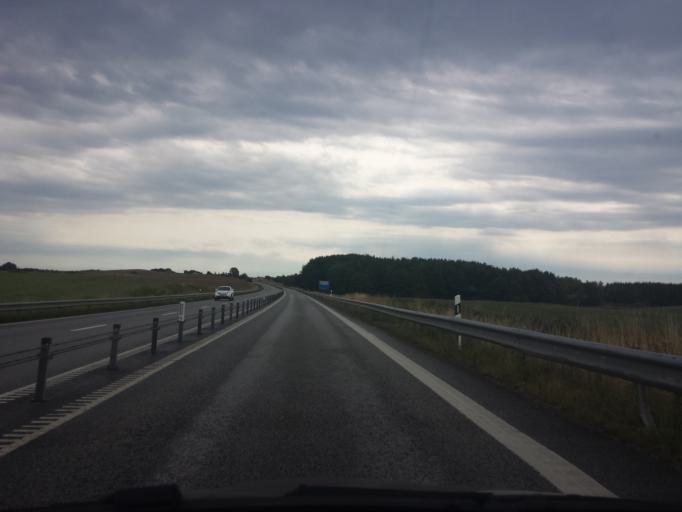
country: SE
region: Skane
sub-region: Ystads Kommun
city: Ystad
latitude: 55.4607
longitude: 13.7272
